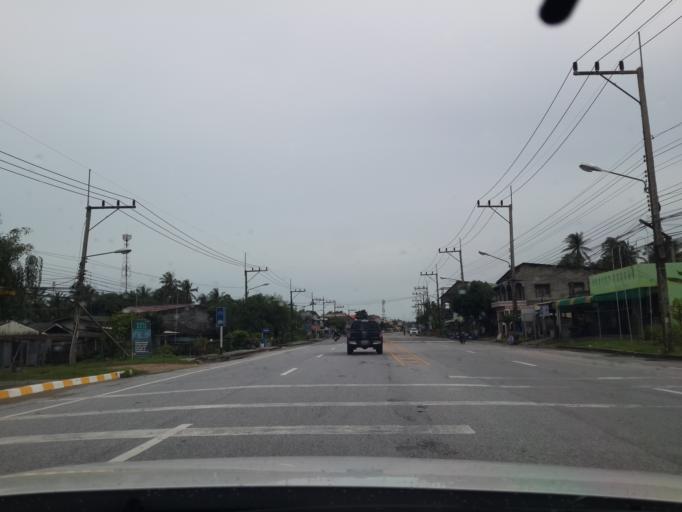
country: TH
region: Pattani
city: Nong Chik
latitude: 6.8384
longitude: 101.1714
